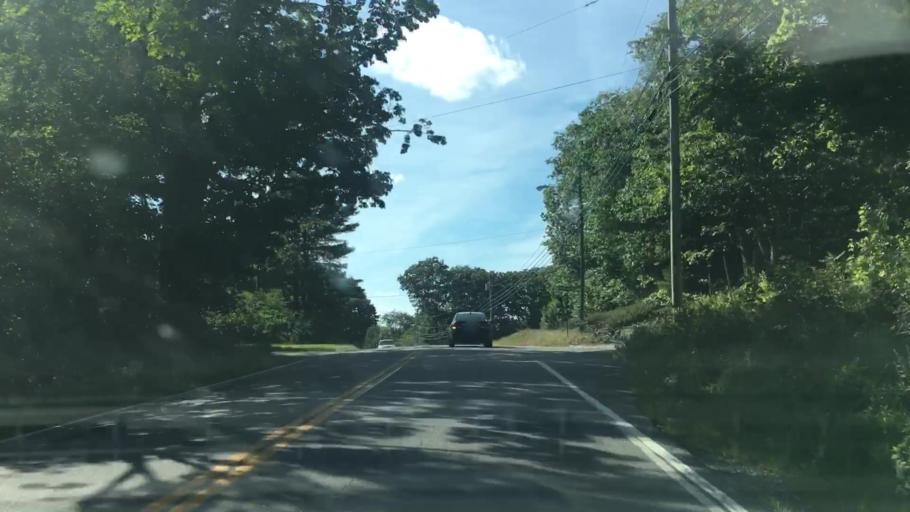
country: US
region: Maine
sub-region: Sagadahoc County
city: North Bath
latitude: 43.9331
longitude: -69.8679
